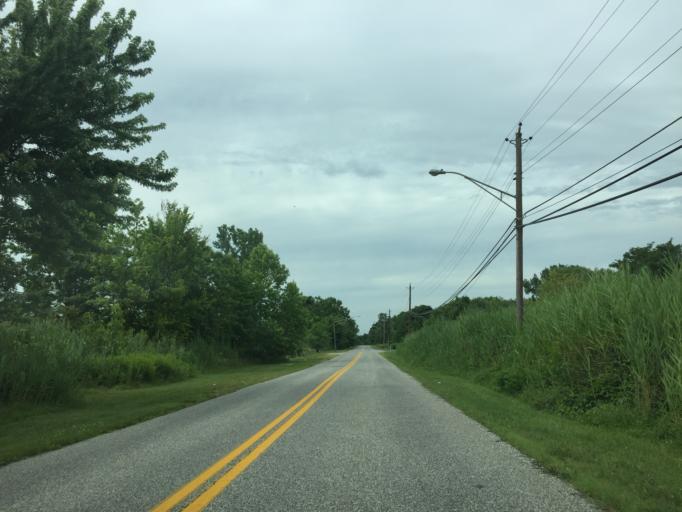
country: US
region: Maryland
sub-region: Baltimore County
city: Edgemere
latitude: 39.2541
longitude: -76.4554
